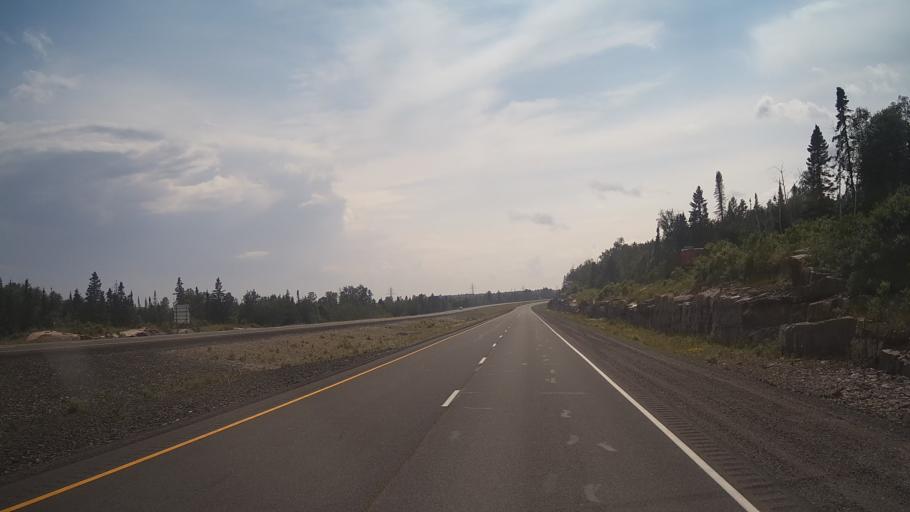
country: CA
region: Ontario
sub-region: Thunder Bay District
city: Thunder Bay
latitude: 48.5491
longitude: -88.9108
